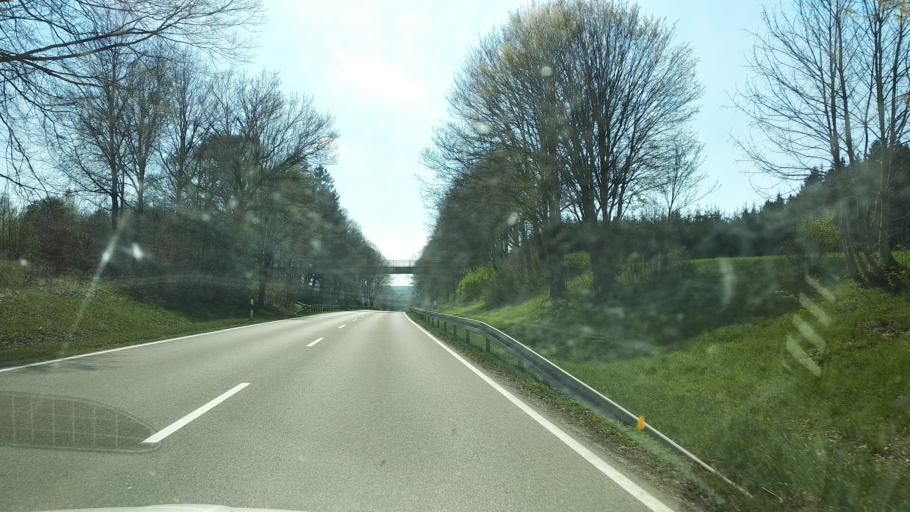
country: DE
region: Bavaria
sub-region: Swabia
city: Erkheim
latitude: 48.0367
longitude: 10.3596
